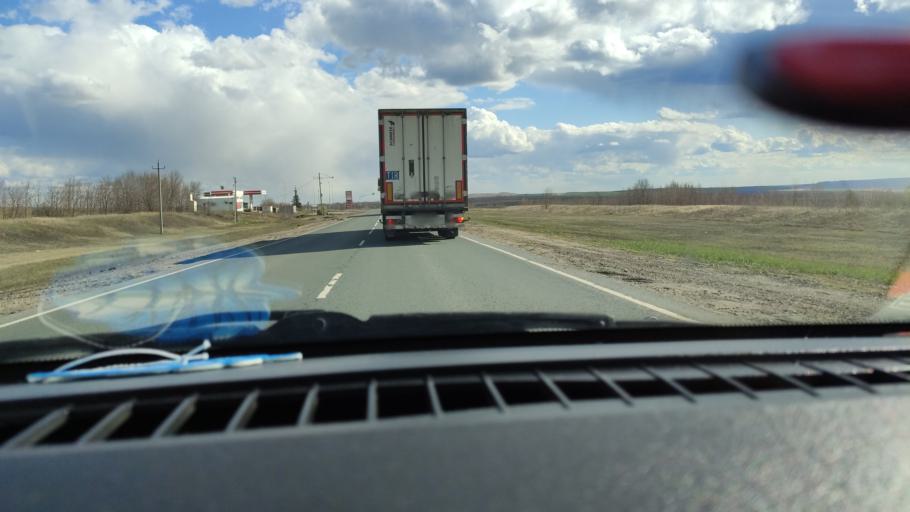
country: RU
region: Saratov
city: Alekseyevka
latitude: 52.2919
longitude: 47.9294
